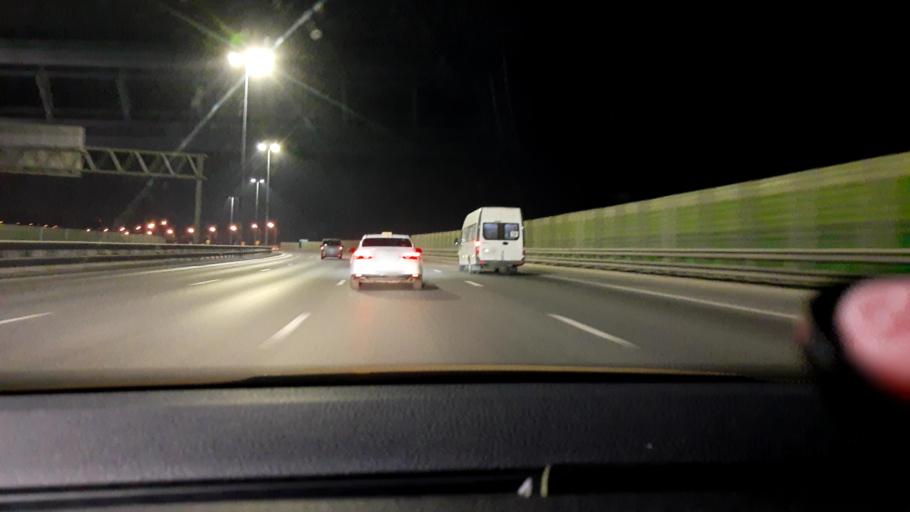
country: RU
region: Moskovskaya
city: Nemchinovka
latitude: 55.7310
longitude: 37.3573
